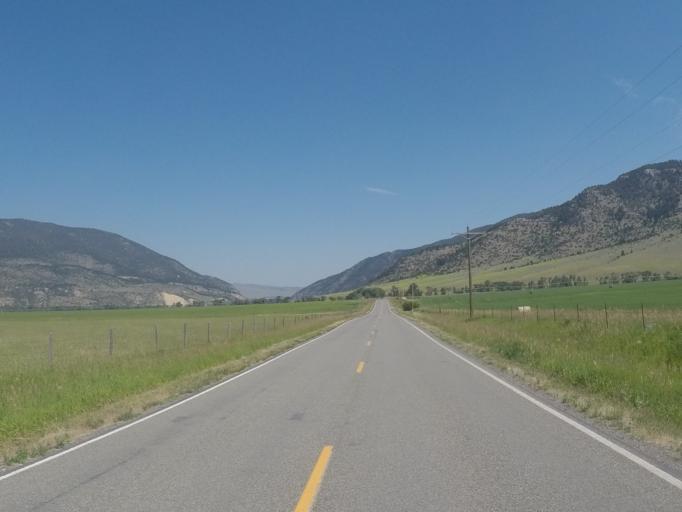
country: US
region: Montana
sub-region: Park County
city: Livingston
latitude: 45.5595
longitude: -110.5589
